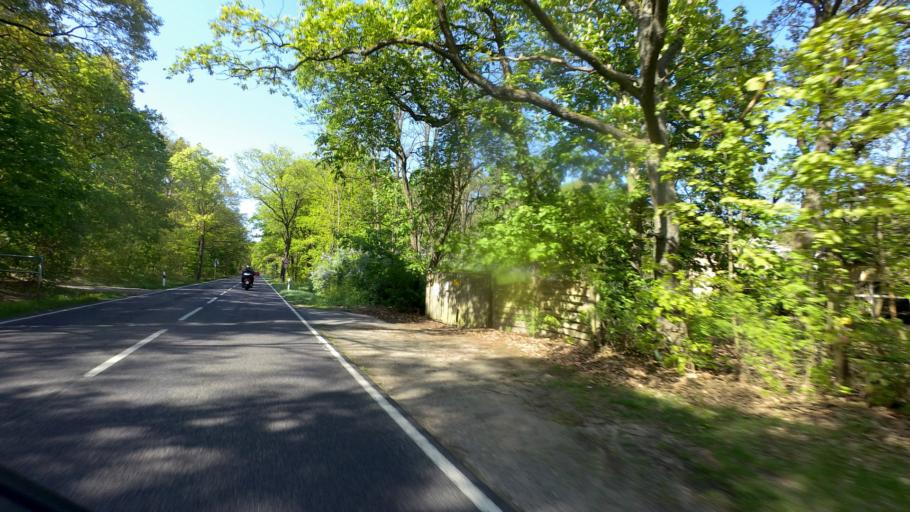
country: DE
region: Brandenburg
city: Bestensee
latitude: 52.2180
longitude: 13.6862
